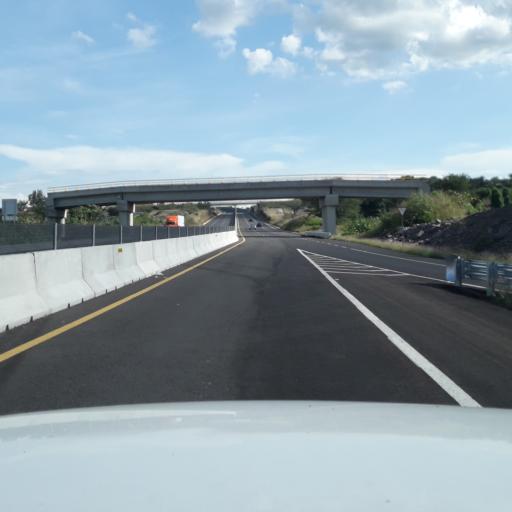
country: MX
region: Jalisco
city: Arenal
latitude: 20.7915
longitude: -103.7124
